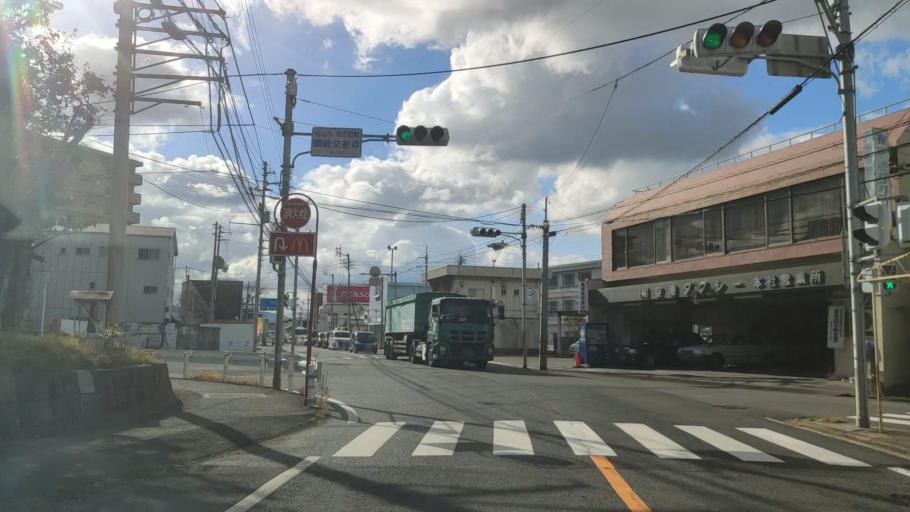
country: JP
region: Ehime
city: Masaki-cho
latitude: 33.8301
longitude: 132.7085
